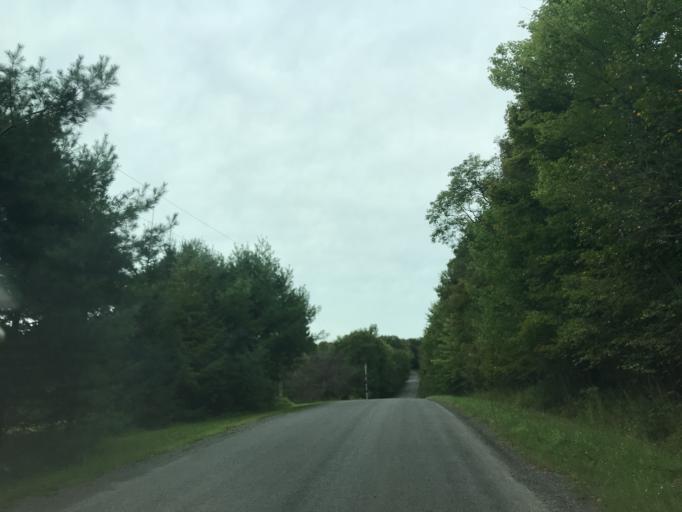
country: US
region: New York
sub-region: Otsego County
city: Worcester
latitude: 42.5236
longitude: -74.6631
